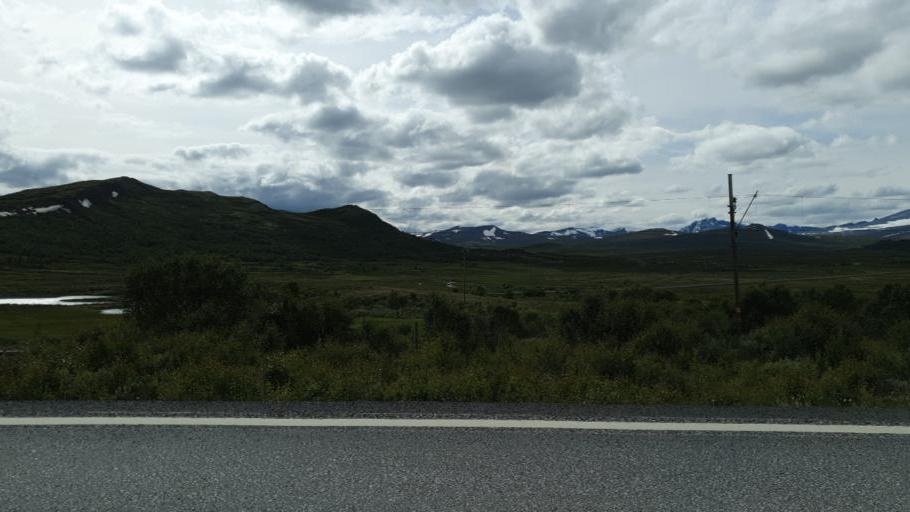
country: NO
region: Oppland
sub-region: Dovre
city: Dovre
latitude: 62.2360
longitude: 9.5296
